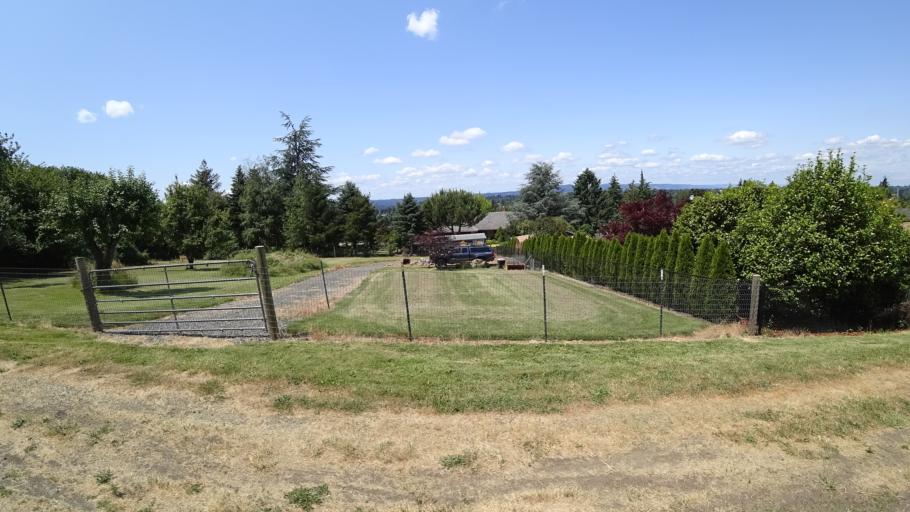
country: US
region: Oregon
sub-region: Multnomah County
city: Lents
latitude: 45.4607
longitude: -122.5649
